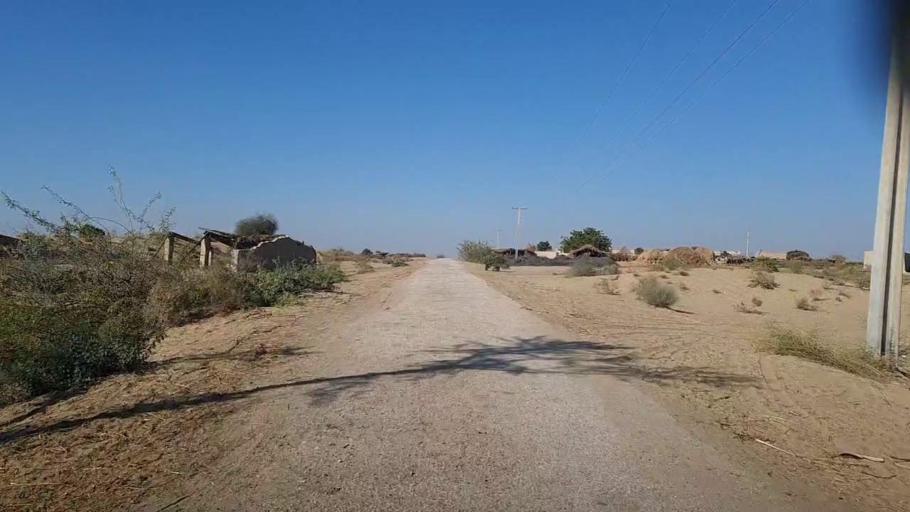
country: PK
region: Sindh
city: Khairpur
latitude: 27.9213
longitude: 69.7507
